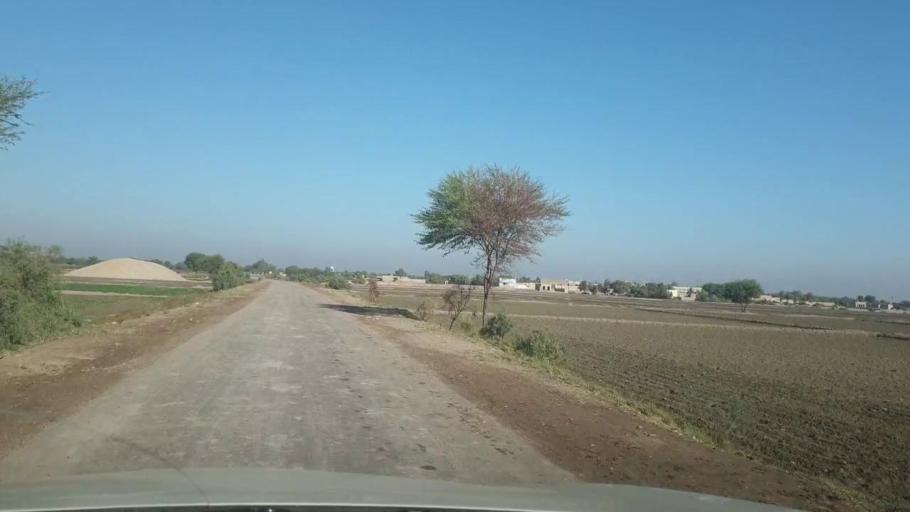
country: PK
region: Sindh
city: Bhan
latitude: 26.5322
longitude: 67.6745
